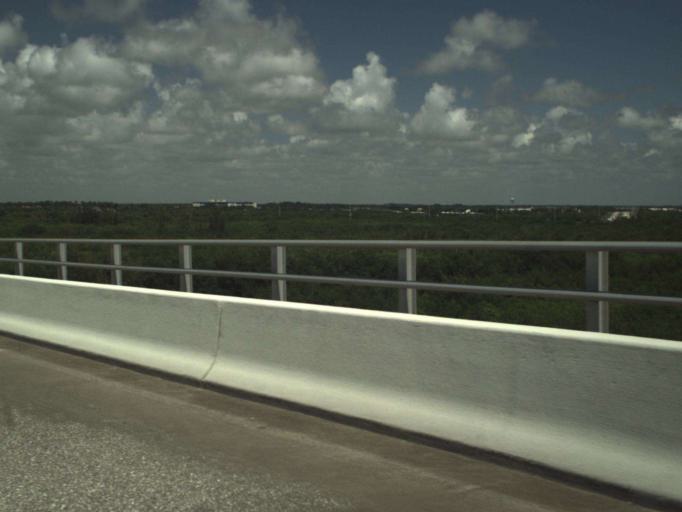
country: US
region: Florida
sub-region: Indian River County
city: Vero Beach
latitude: 27.6526
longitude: -80.3772
